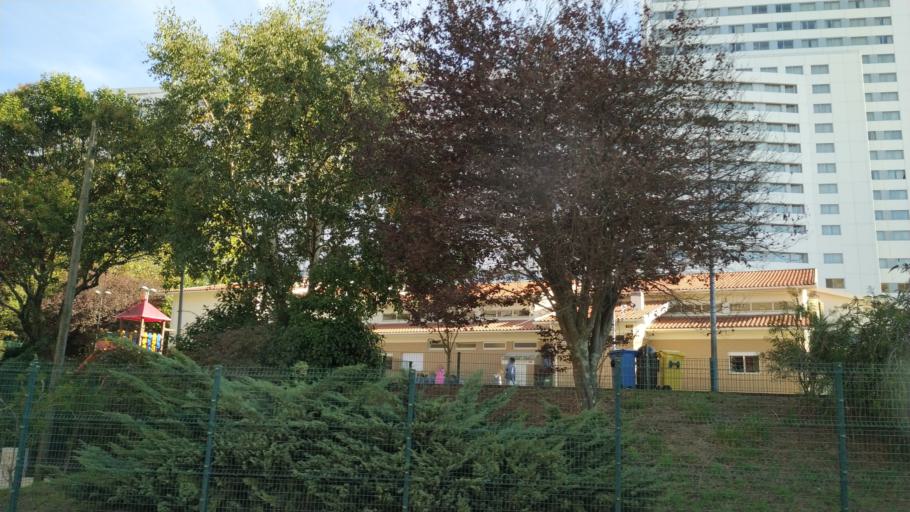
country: PT
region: Porto
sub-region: Vila Nova de Gaia
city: Vila Nova de Gaia
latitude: 41.1254
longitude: -8.6150
